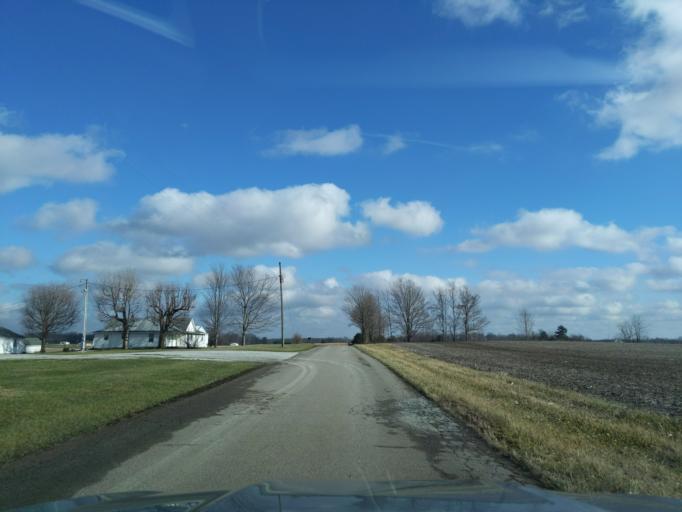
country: US
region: Indiana
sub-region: Decatur County
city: Greensburg
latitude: 39.2781
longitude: -85.4575
